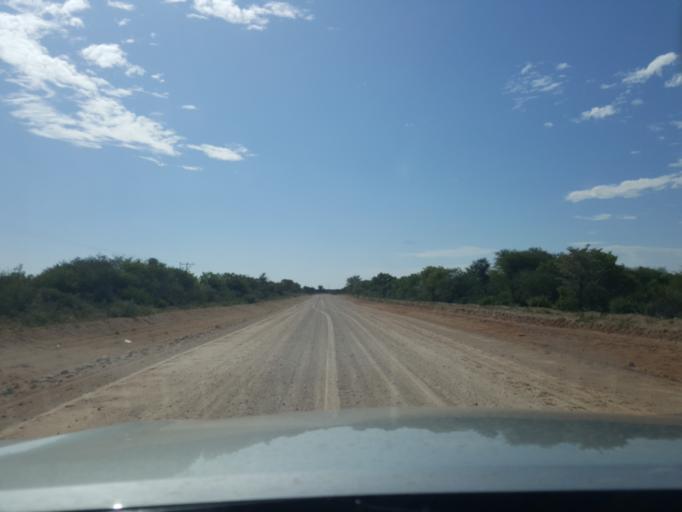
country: BW
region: Kweneng
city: Khudumelapye
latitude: -23.7819
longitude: 24.7758
